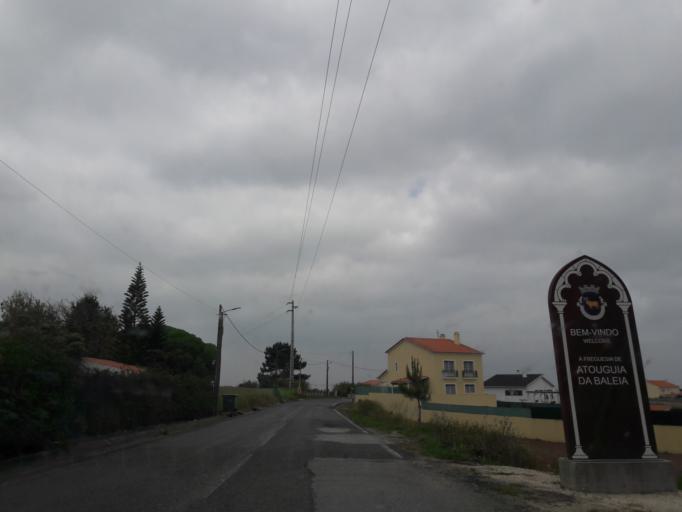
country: PT
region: Leiria
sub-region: Peniche
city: Atouguia da Baleia
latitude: 39.3466
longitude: -9.2847
